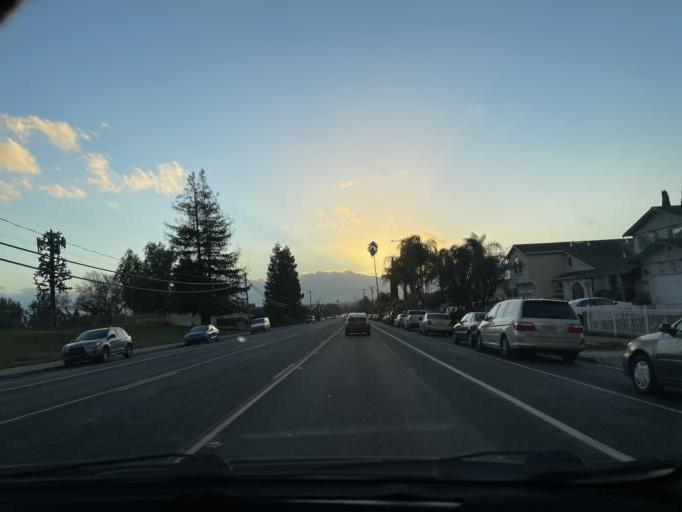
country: US
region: California
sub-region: Santa Clara County
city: Alum Rock
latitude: 37.3493
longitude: -121.7995
